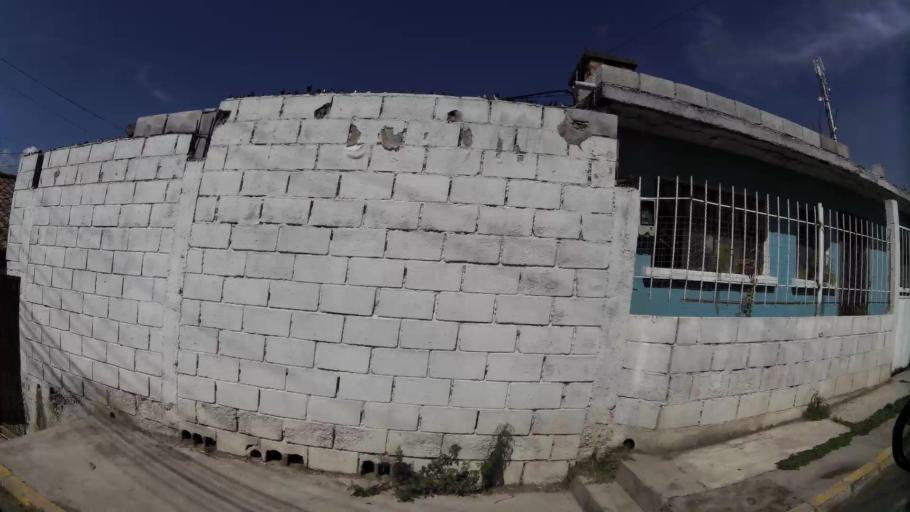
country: EC
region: Pichincha
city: Quito
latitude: -0.2033
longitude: -78.4415
